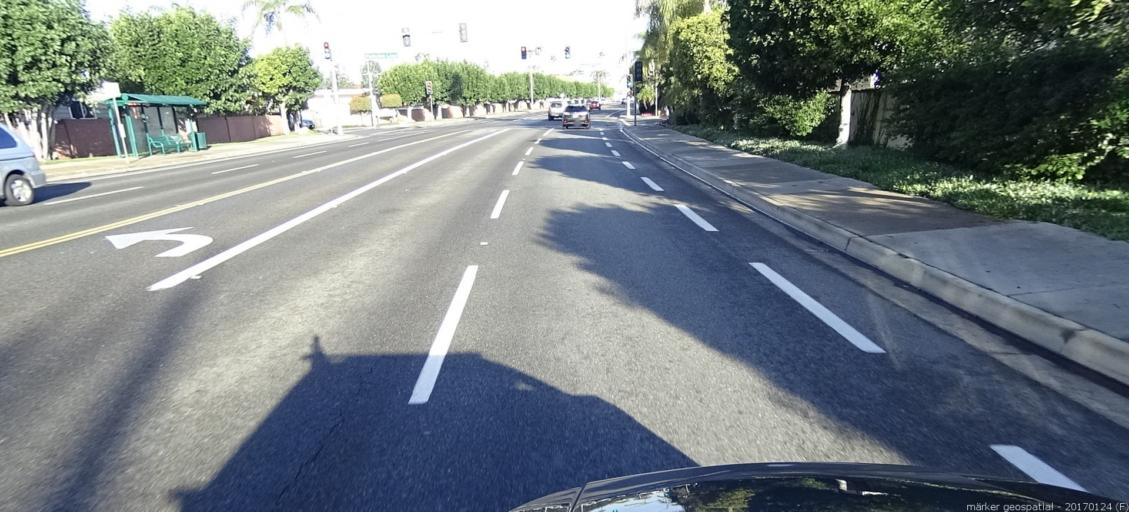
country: US
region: California
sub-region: Orange County
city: Laguna Hills
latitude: 33.6189
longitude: -117.6942
